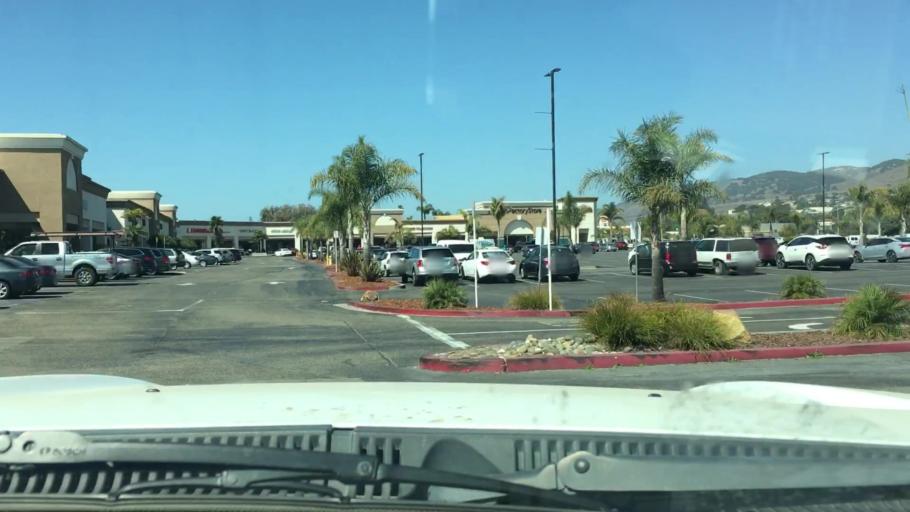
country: US
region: California
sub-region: San Luis Obispo County
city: Grover Beach
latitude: 35.1356
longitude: -120.6274
